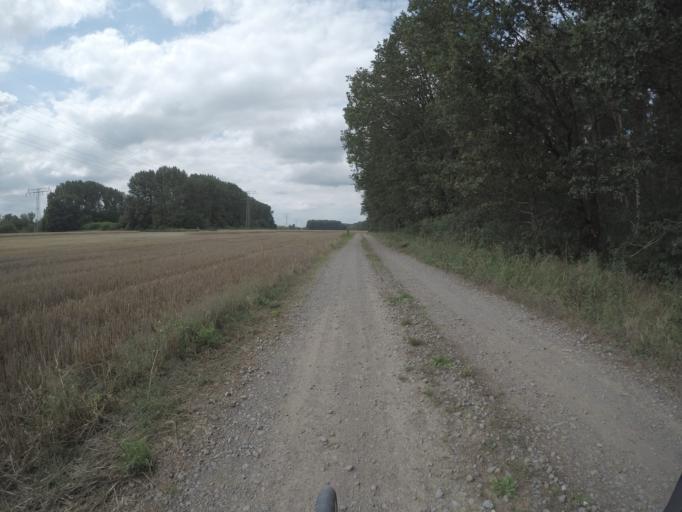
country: DE
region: Brandenburg
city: Brieselang
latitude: 52.6131
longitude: 13.0387
